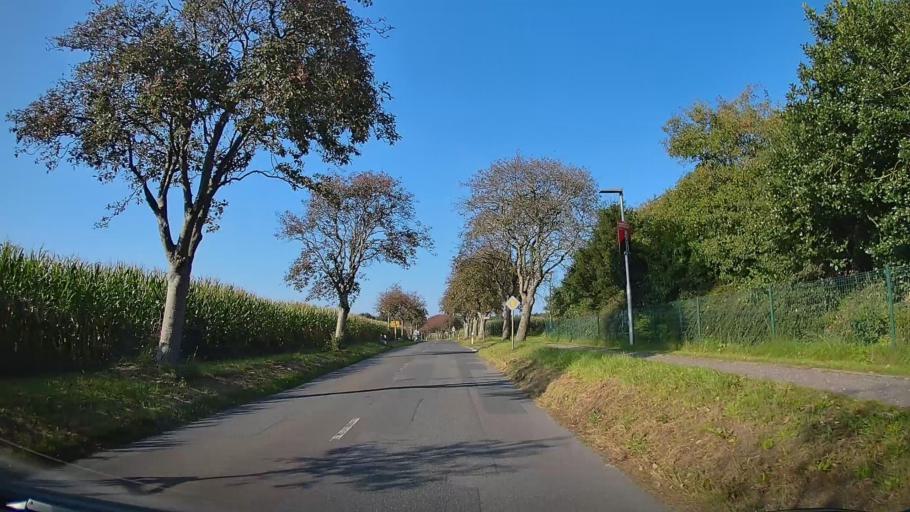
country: DE
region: Lower Saxony
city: Nordholz
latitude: 53.7993
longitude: 8.6100
